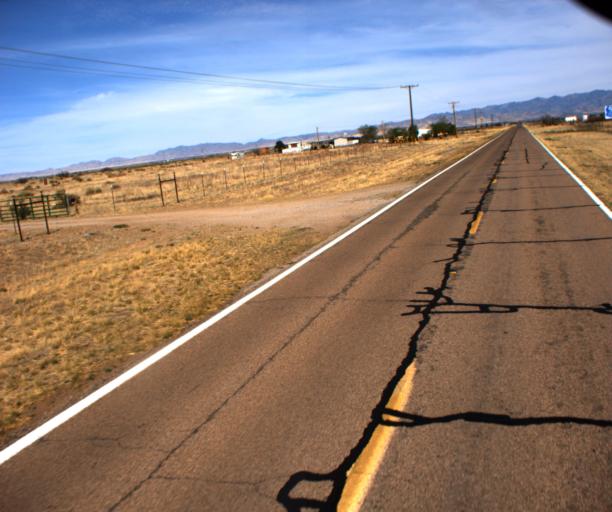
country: US
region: Arizona
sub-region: Cochise County
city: Willcox
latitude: 31.8837
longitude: -109.6814
